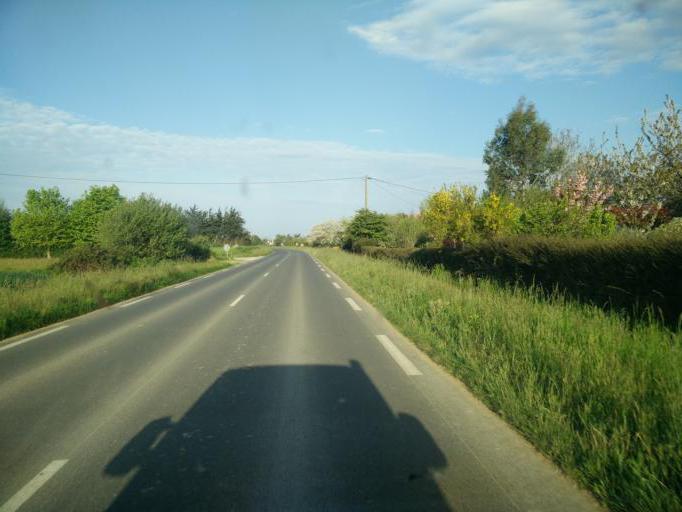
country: FR
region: Brittany
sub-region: Departement des Cotes-d'Armor
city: Plurien
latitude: 48.6261
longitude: -2.3808
